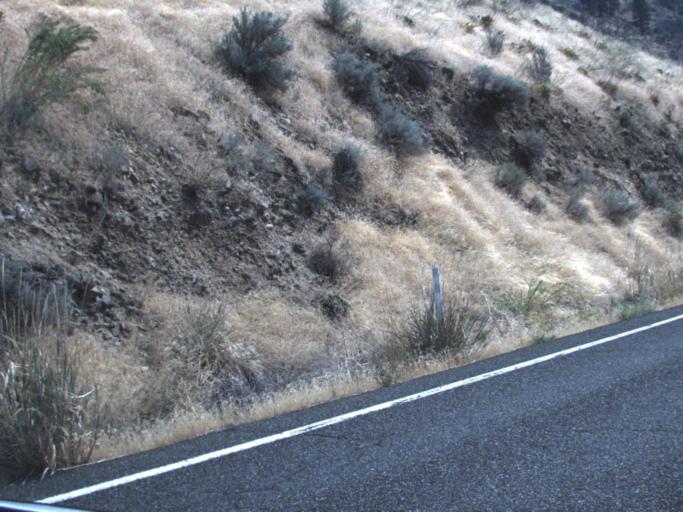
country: US
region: Washington
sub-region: Kittitas County
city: Kittitas
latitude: 46.8824
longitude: -120.4746
